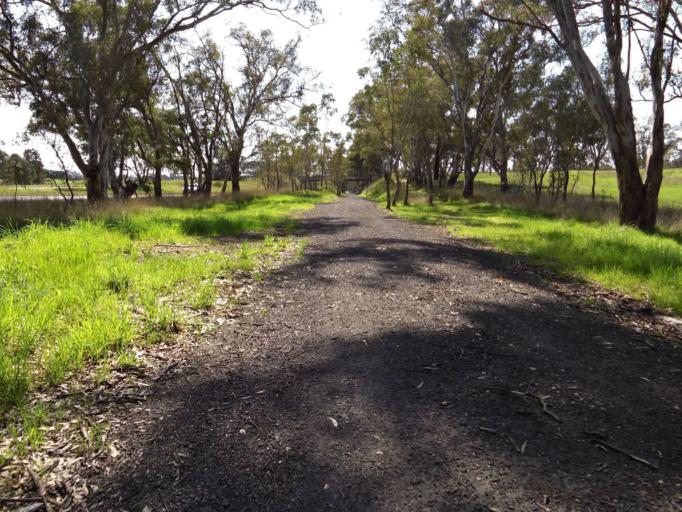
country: AU
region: Victoria
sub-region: Murrindindi
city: Alexandra
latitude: -37.1178
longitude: 145.6047
